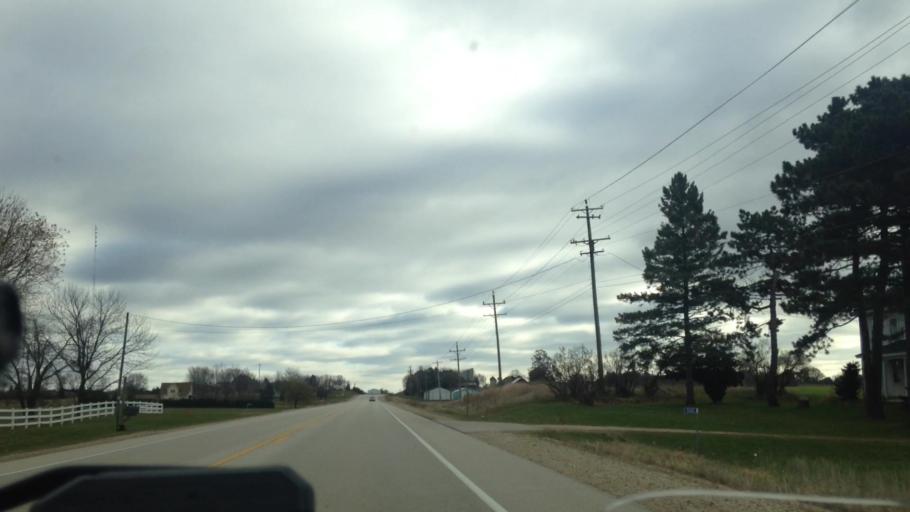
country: US
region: Wisconsin
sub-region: Washington County
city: Slinger
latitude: 43.4274
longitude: -88.3093
